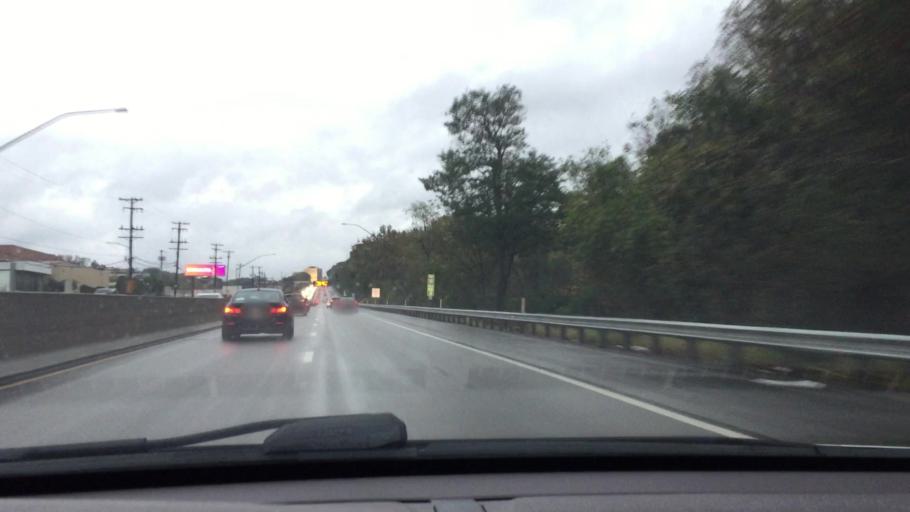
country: US
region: Pennsylvania
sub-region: Allegheny County
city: Carnegie
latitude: 40.4118
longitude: -80.0680
